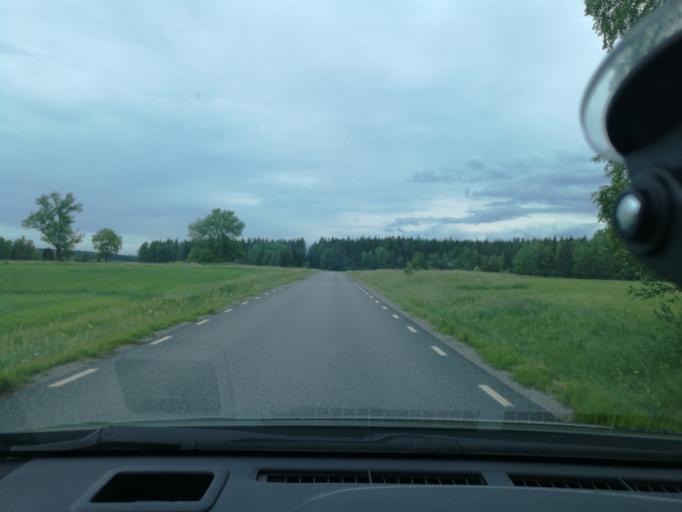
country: SE
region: Vaestmanland
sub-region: Surahammars Kommun
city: Ramnas
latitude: 59.8289
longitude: 16.3165
